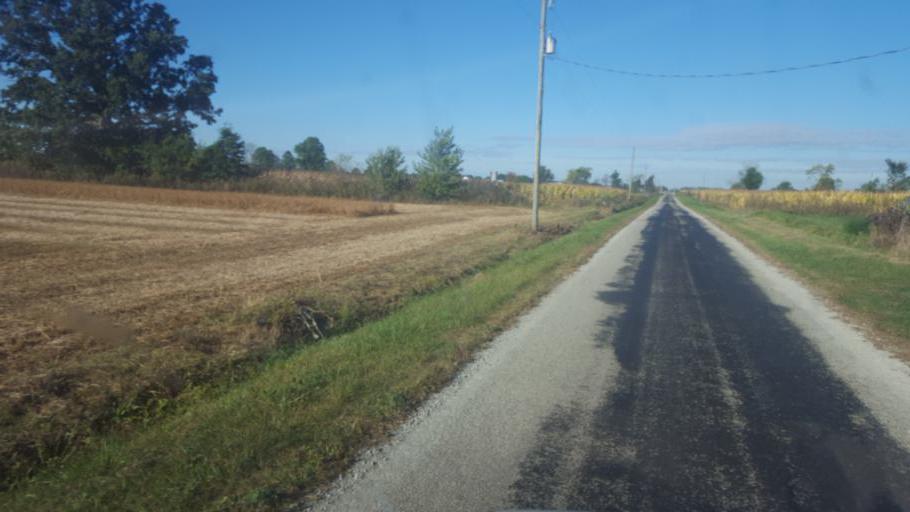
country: US
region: Ohio
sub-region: Crawford County
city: Galion
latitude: 40.6901
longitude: -82.8993
